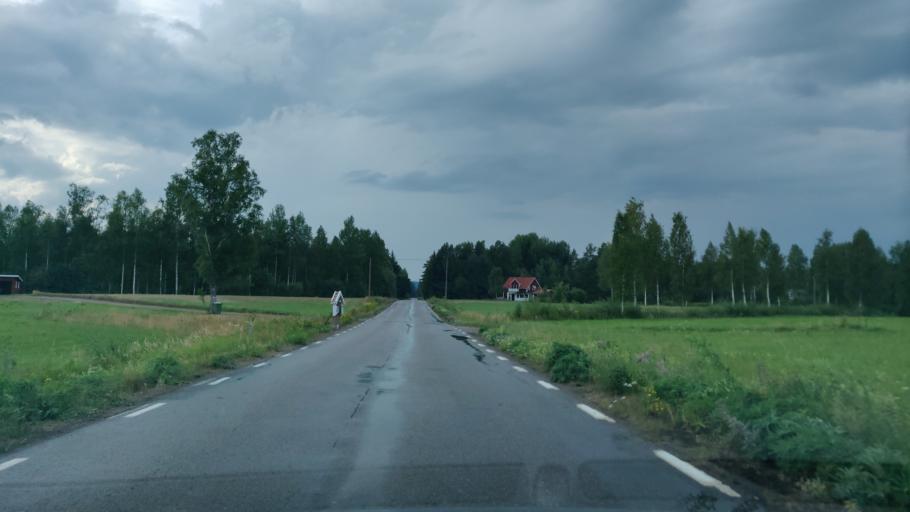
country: SE
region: Vaermland
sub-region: Munkfors Kommun
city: Munkfors
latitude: 59.8699
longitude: 13.5357
